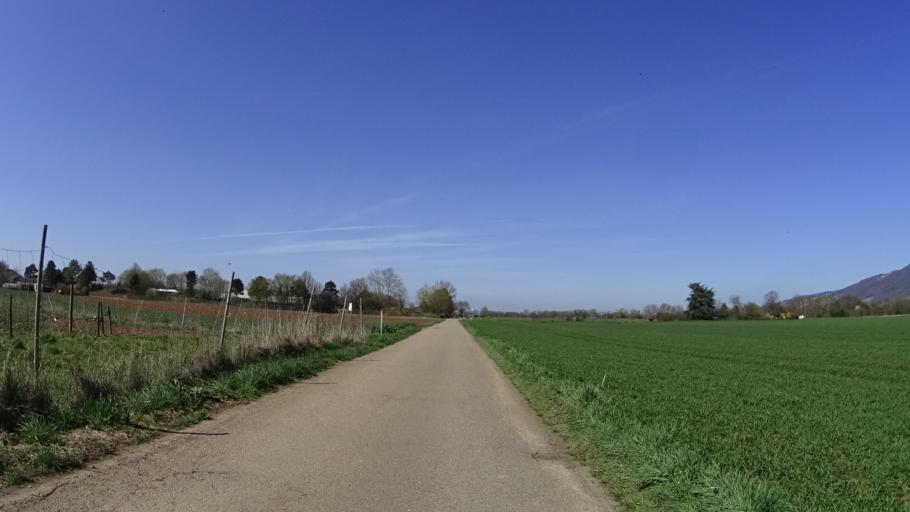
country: DE
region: Baden-Wuerttemberg
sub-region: Karlsruhe Region
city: Dossenheim
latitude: 49.4329
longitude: 8.6556
